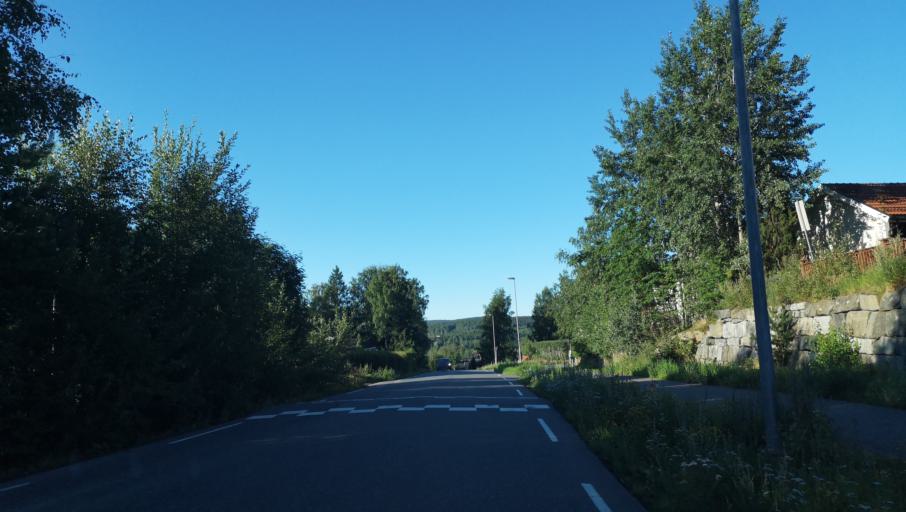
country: NO
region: Ostfold
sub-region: Hobol
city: Knappstad
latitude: 59.6289
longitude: 11.0273
